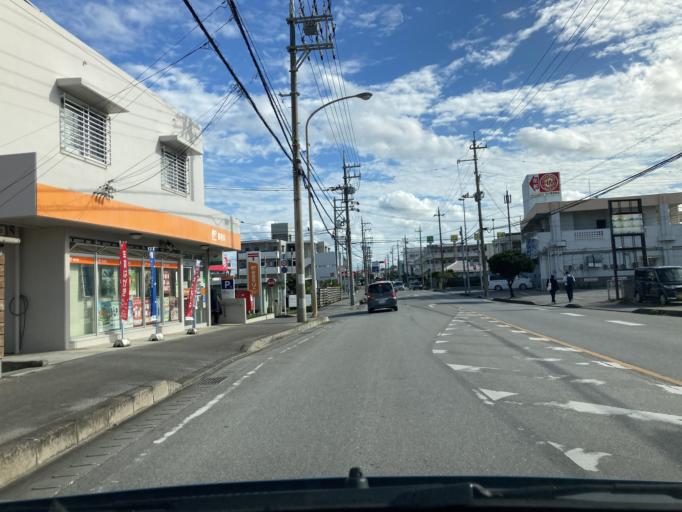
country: JP
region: Okinawa
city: Ishikawa
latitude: 26.4140
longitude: 127.8234
